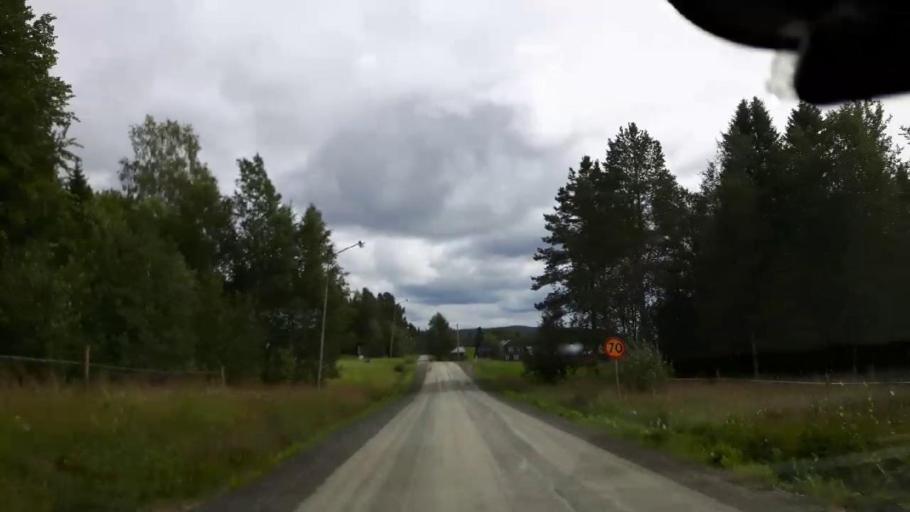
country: SE
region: Jaemtland
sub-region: Krokoms Kommun
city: Valla
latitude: 63.6177
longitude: 14.0719
